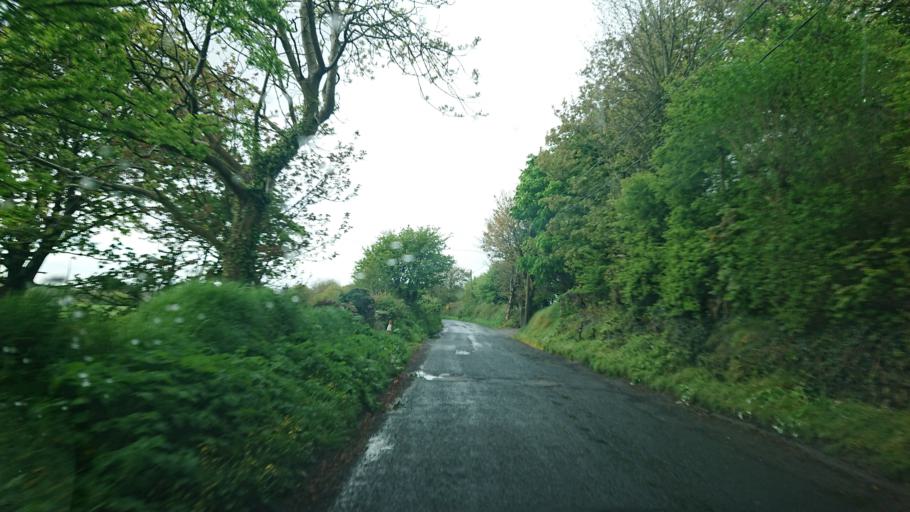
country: IE
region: Munster
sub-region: Waterford
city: Waterford
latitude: 52.2266
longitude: -7.0724
